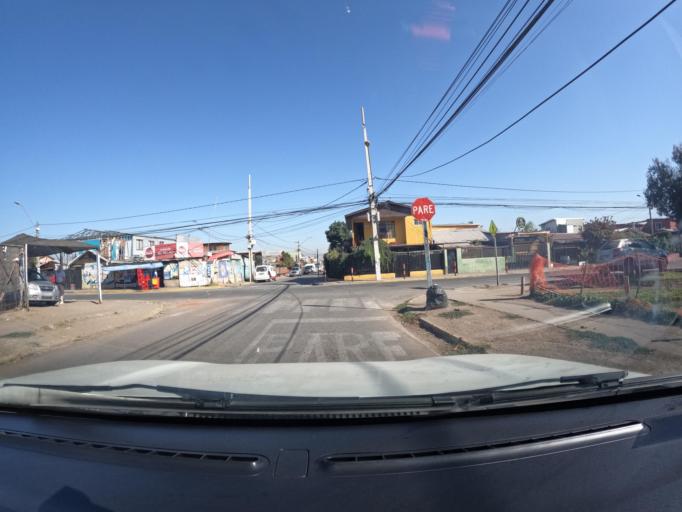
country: CL
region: Santiago Metropolitan
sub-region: Provincia de Santiago
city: Villa Presidente Frei, Nunoa, Santiago, Chile
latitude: -33.4780
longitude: -70.5724
